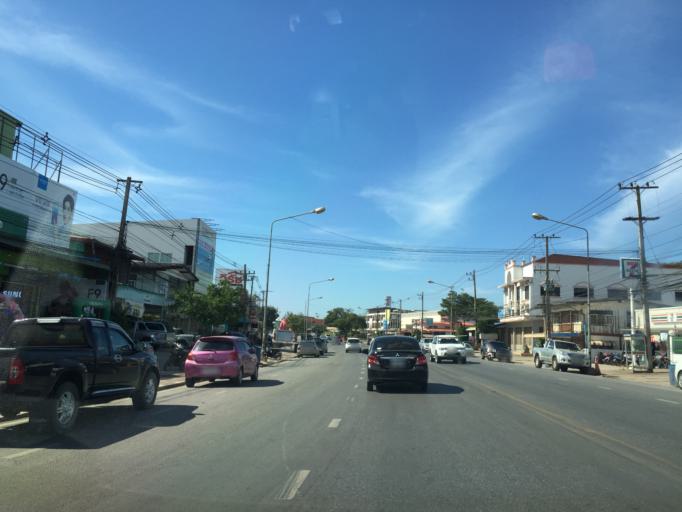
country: TH
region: Changwat Nong Bua Lamphu
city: Na Klang
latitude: 17.3020
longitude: 102.2038
